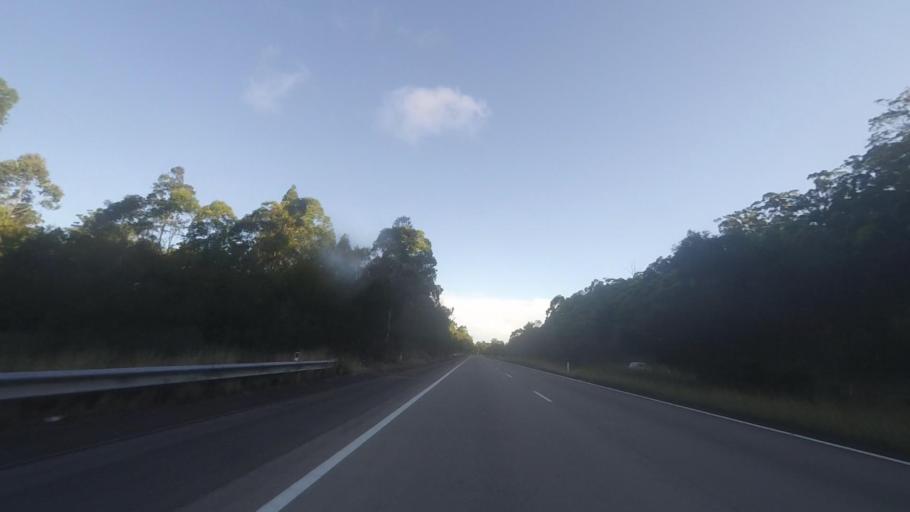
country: AU
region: New South Wales
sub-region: Great Lakes
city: Bulahdelah
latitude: -32.2950
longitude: 152.3444
